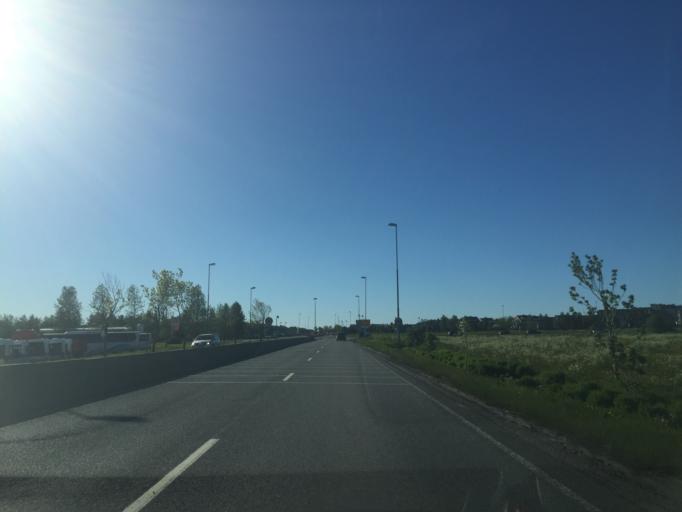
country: NO
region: Nordland
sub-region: Bodo
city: Bodo
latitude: 67.2803
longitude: 14.4248
